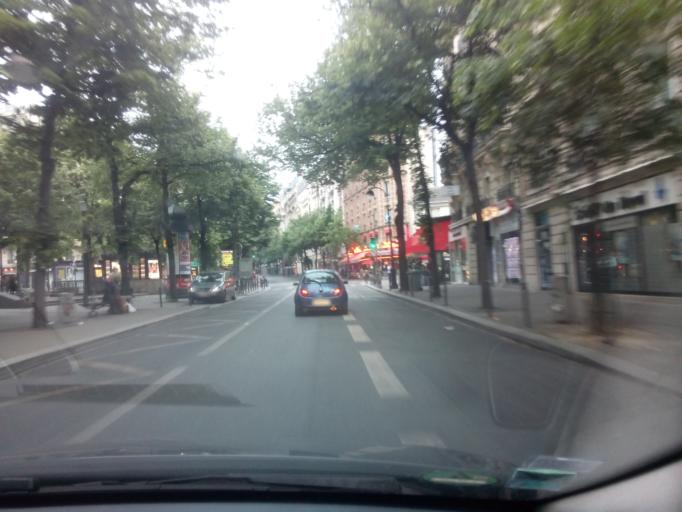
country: FR
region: Ile-de-France
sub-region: Departement des Hauts-de-Seine
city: Vanves
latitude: 48.8376
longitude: 2.2955
